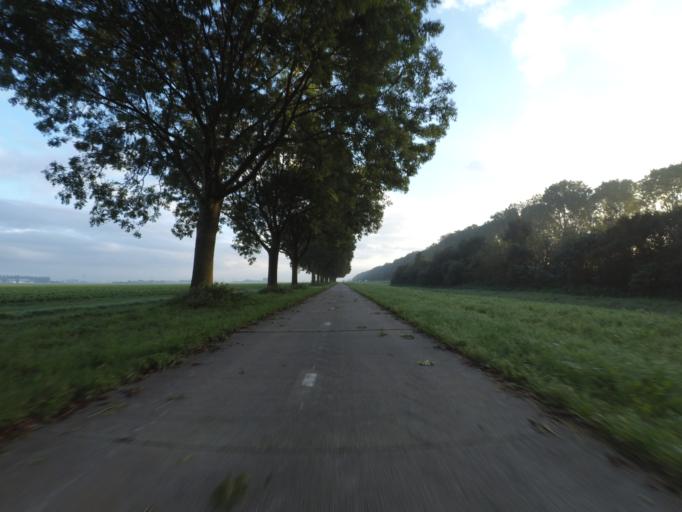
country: NL
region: Gelderland
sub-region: Gemeente Harderwijk
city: Harderwijk
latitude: 52.4124
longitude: 5.6039
